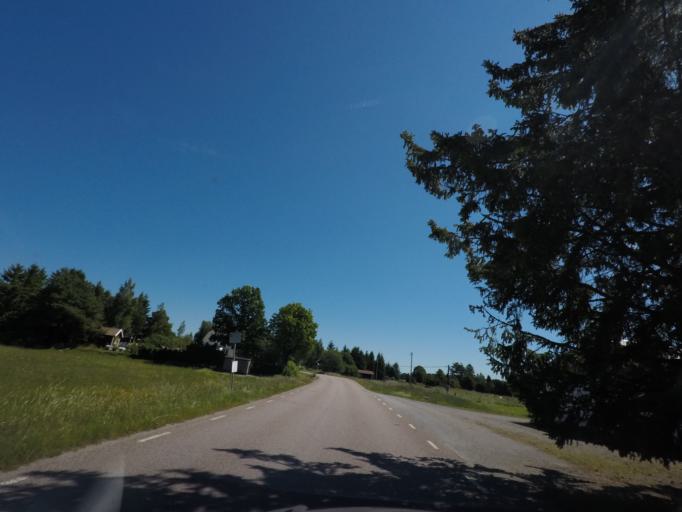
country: SE
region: Uppsala
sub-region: Enkopings Kommun
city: Irsta
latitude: 59.6812
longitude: 16.8154
